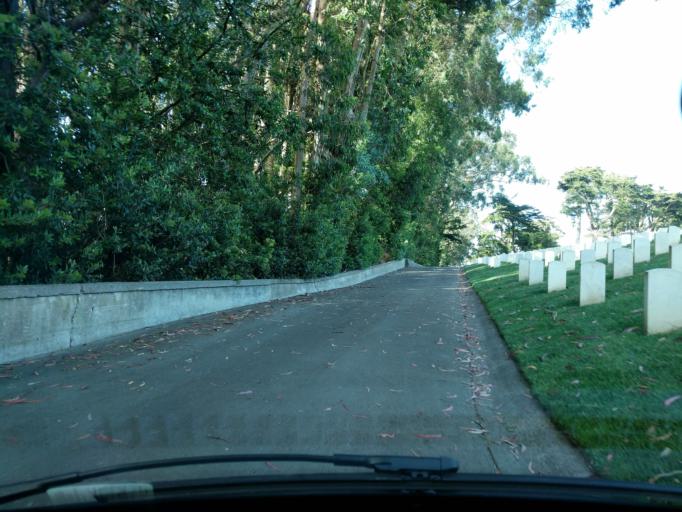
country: US
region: California
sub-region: San Francisco County
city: San Francisco
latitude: 37.7995
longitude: -122.4662
